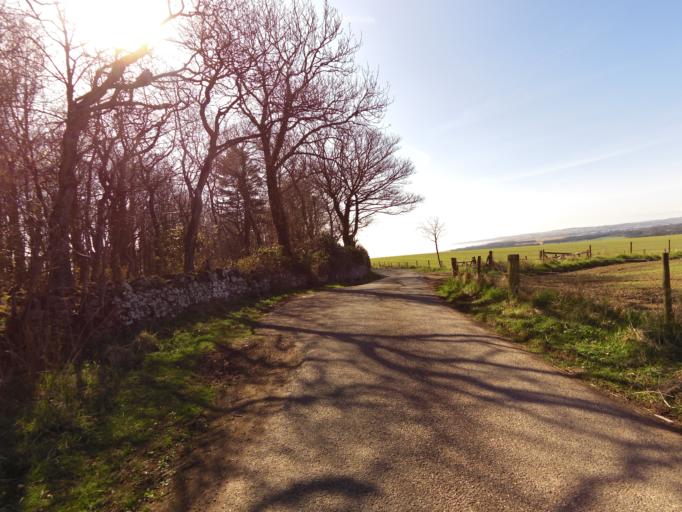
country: GB
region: Scotland
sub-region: Angus
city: Montrose
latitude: 56.7663
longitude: -2.4322
